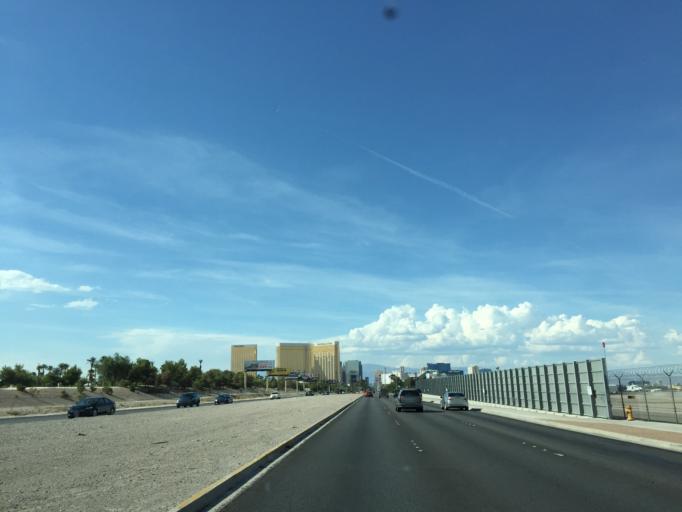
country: US
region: Nevada
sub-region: Clark County
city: Paradise
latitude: 36.0756
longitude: -115.1725
